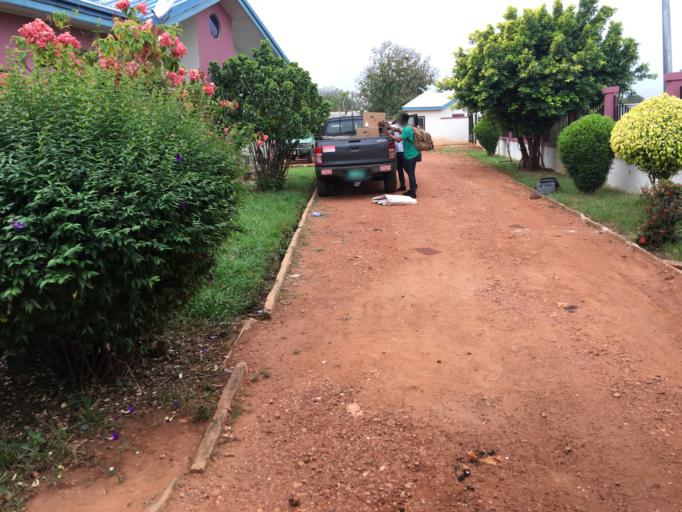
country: GH
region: Brong-Ahafo
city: Wenchi
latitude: 7.8702
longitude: -2.3223
